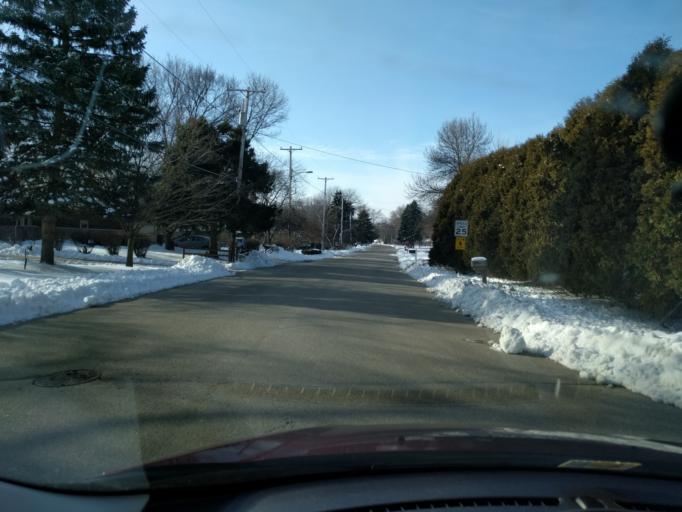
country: US
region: Wisconsin
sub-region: Milwaukee County
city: Whitefish Bay
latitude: 43.1260
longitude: -87.9151
